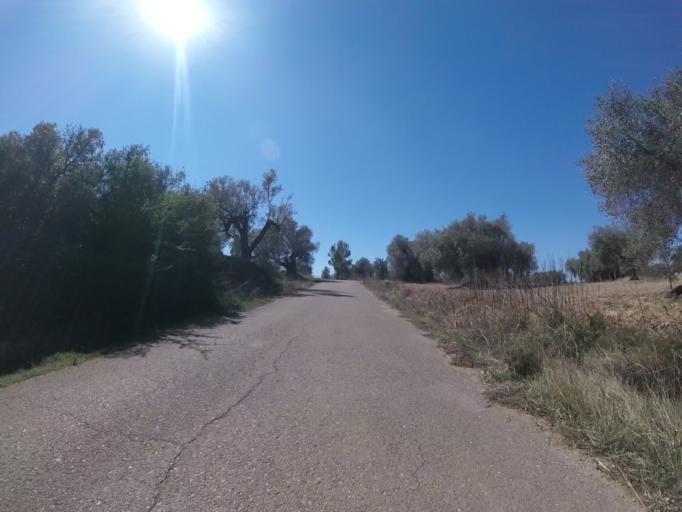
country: ES
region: Valencia
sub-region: Provincia de Castello
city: Cuevas de Vinroma
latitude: 40.3911
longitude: 0.1612
